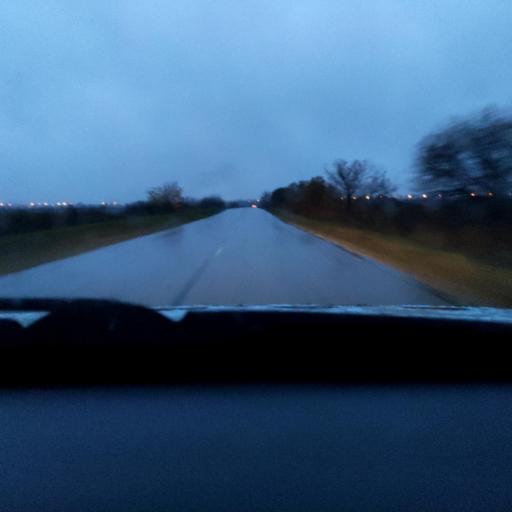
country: RU
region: Perm
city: Kondratovo
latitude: 57.9935
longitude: 56.0898
